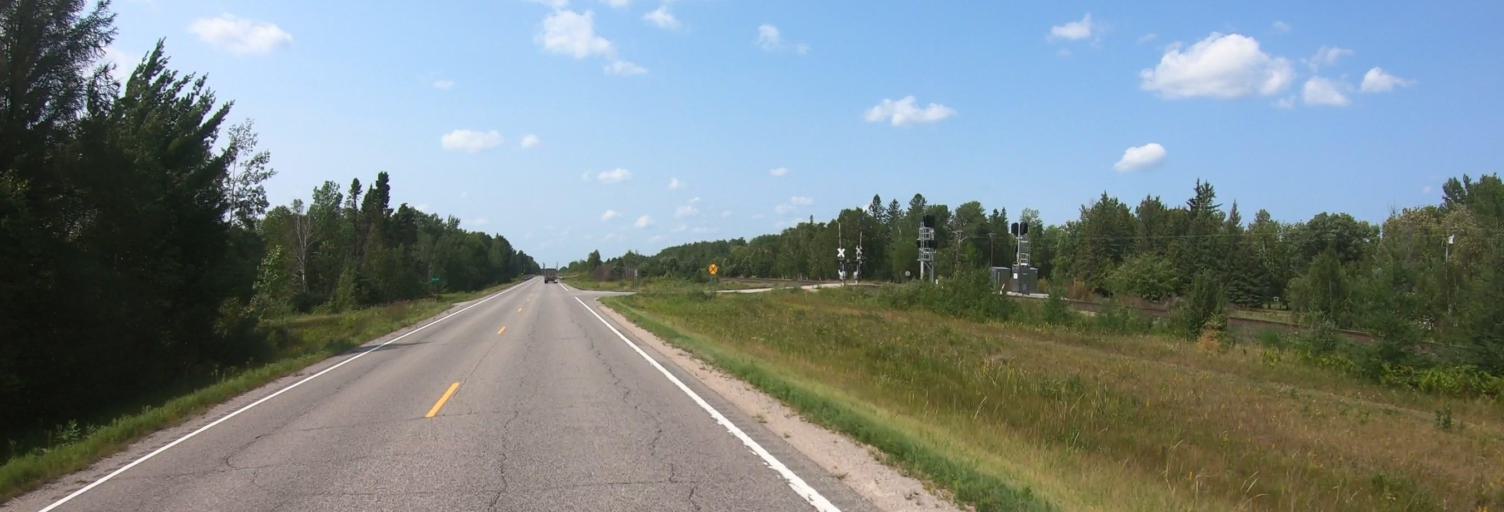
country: US
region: Minnesota
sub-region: Roseau County
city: Warroad
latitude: 48.8081
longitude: -95.1114
